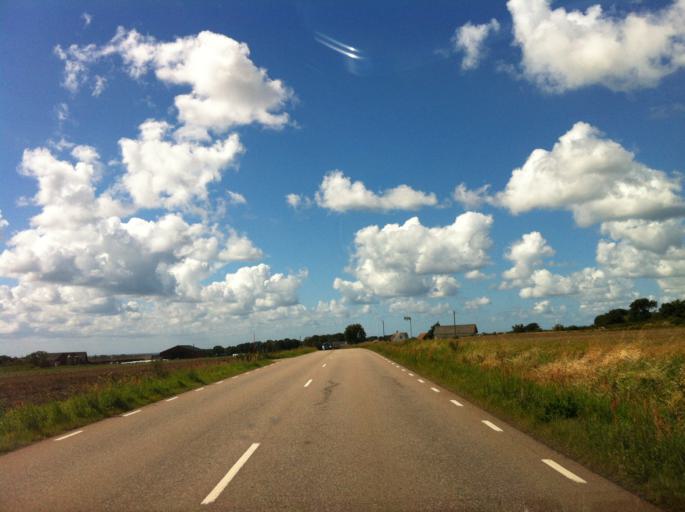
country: SE
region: Skane
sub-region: Angelholms Kommun
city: AEngelholm
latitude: 56.2590
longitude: 12.8838
